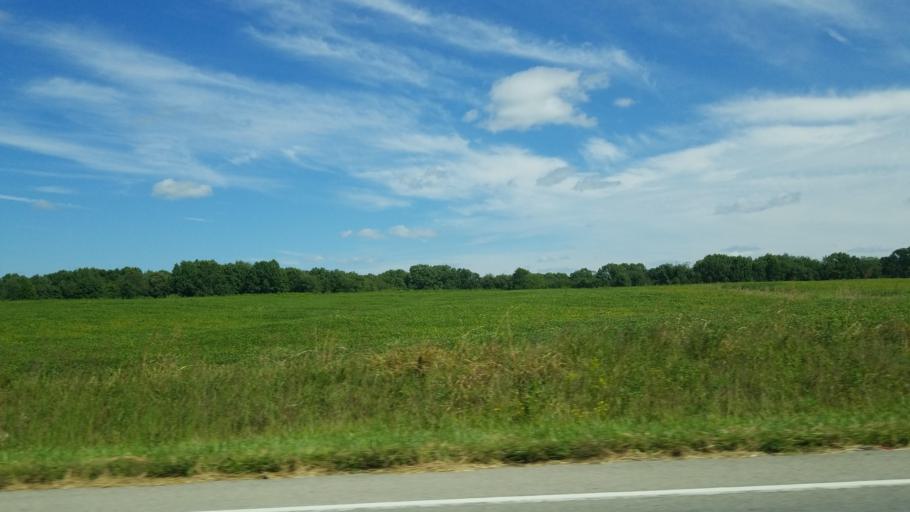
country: US
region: Illinois
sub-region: Williamson County
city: Marion
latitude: 37.7706
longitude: -88.9329
